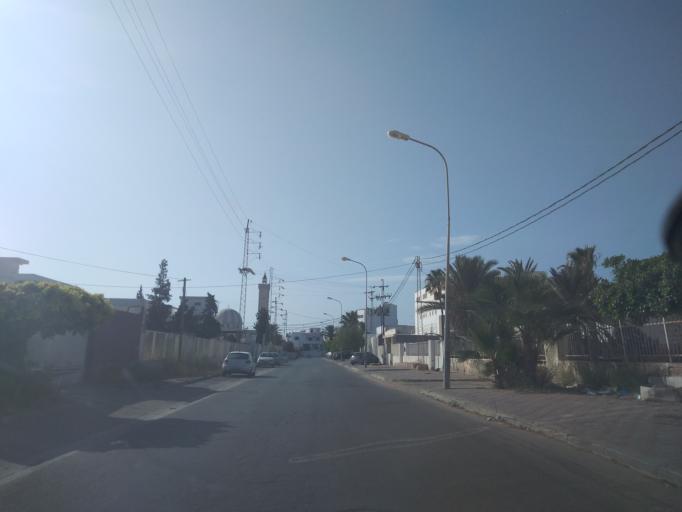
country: TN
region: Safaqis
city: Al Qarmadah
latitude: 34.7489
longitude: 10.7727
